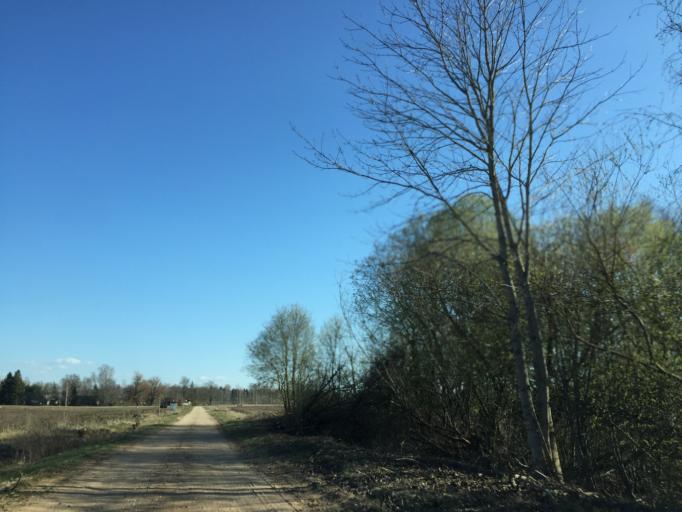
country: EE
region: Valgamaa
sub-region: Torva linn
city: Torva
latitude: 58.2396
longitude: 25.9275
